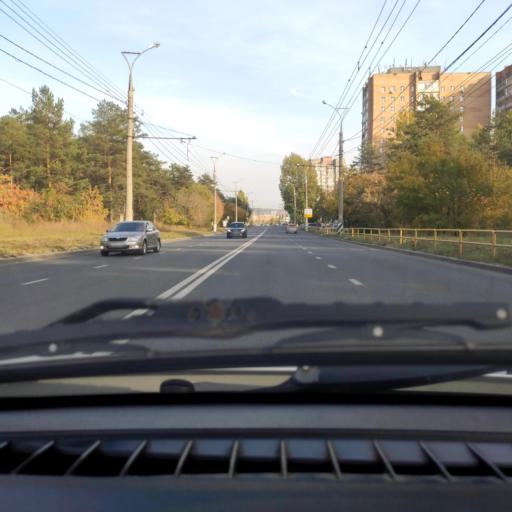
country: RU
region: Samara
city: Zhigulevsk
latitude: 53.4874
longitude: 49.4666
